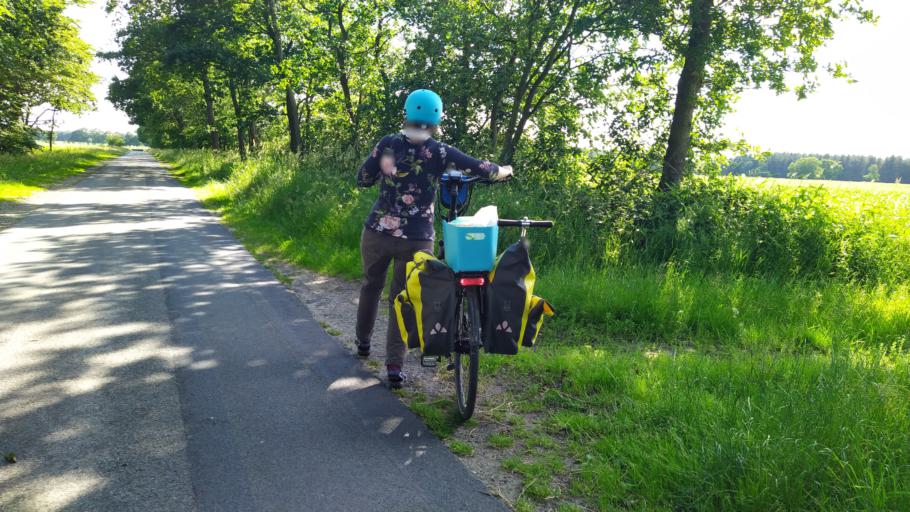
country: DE
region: Lower Saxony
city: Lintig
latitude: 53.6417
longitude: 8.9043
